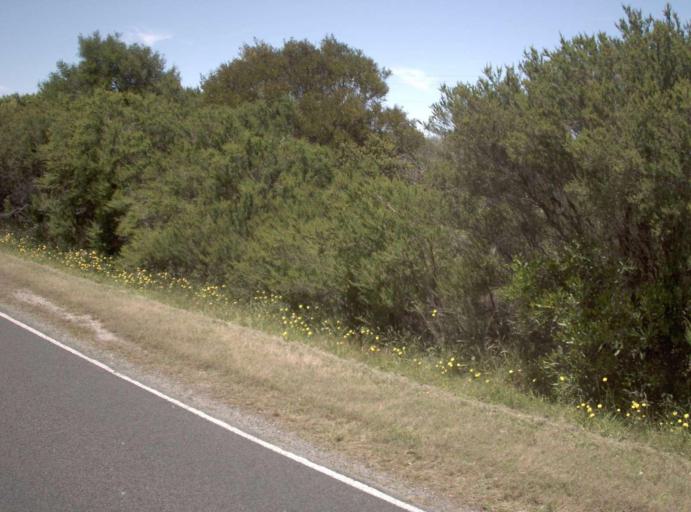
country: AU
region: Victoria
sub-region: Latrobe
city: Morwell
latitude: -38.7888
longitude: 146.1744
